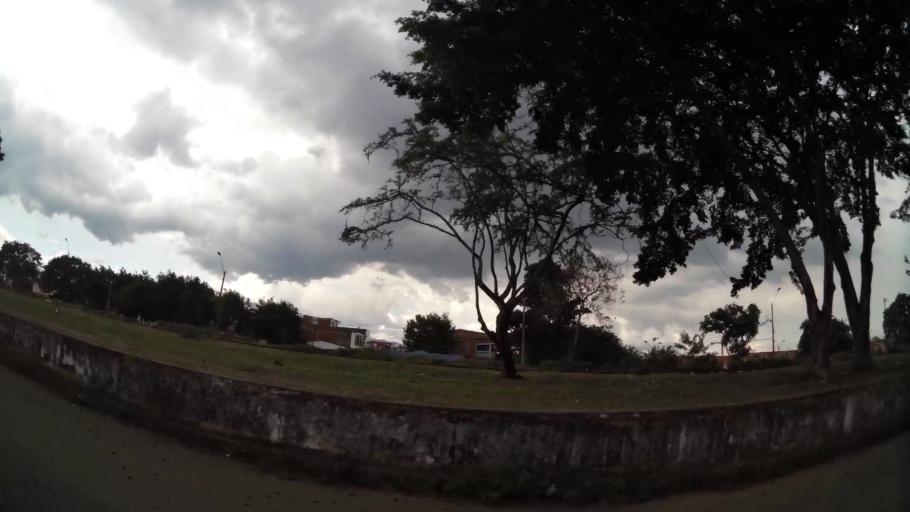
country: CO
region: Valle del Cauca
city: Cali
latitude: 3.4646
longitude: -76.4868
